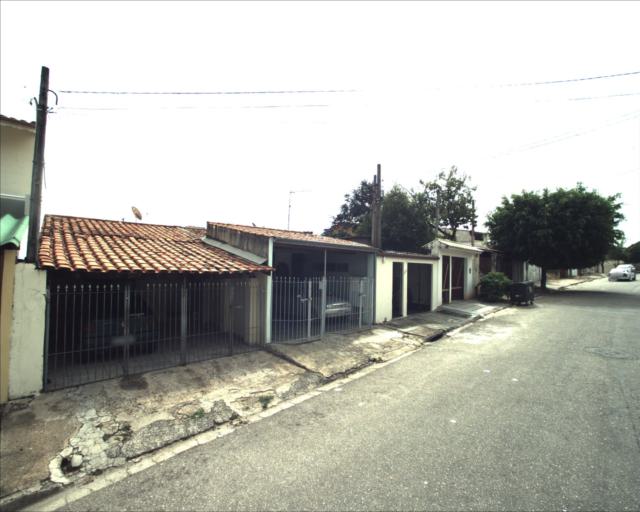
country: BR
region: Sao Paulo
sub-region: Sorocaba
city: Sorocaba
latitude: -23.4962
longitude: -47.4945
